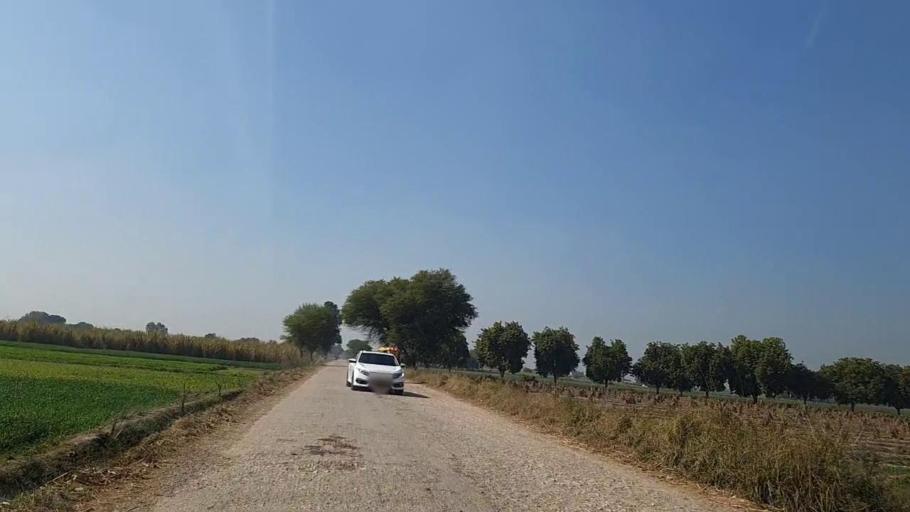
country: PK
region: Sindh
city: Sakrand
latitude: 26.2906
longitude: 68.1007
